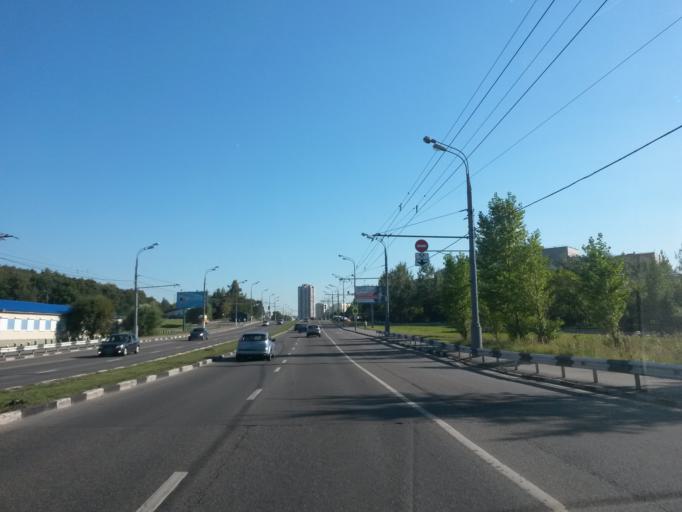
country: RU
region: Moscow
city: Yasenevo
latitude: 55.6282
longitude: 37.5406
